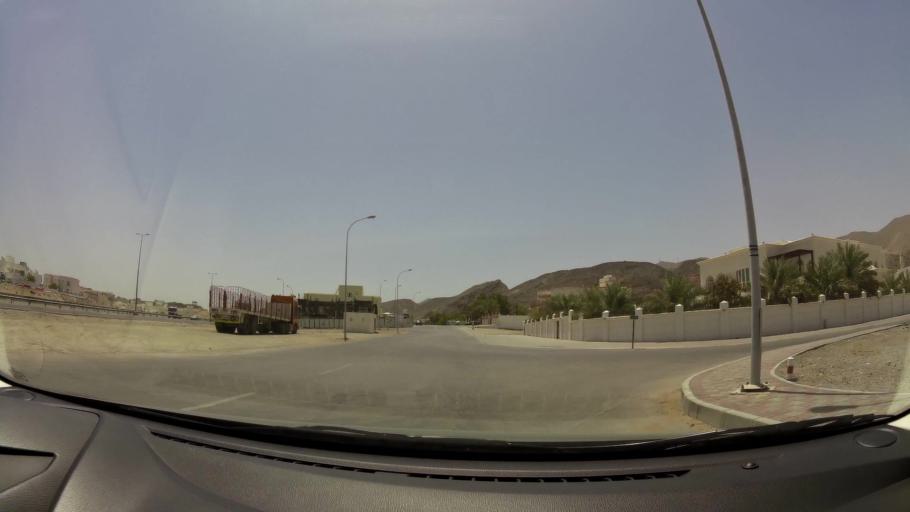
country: OM
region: Muhafazat Masqat
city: Bawshar
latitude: 23.5896
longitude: 58.4532
